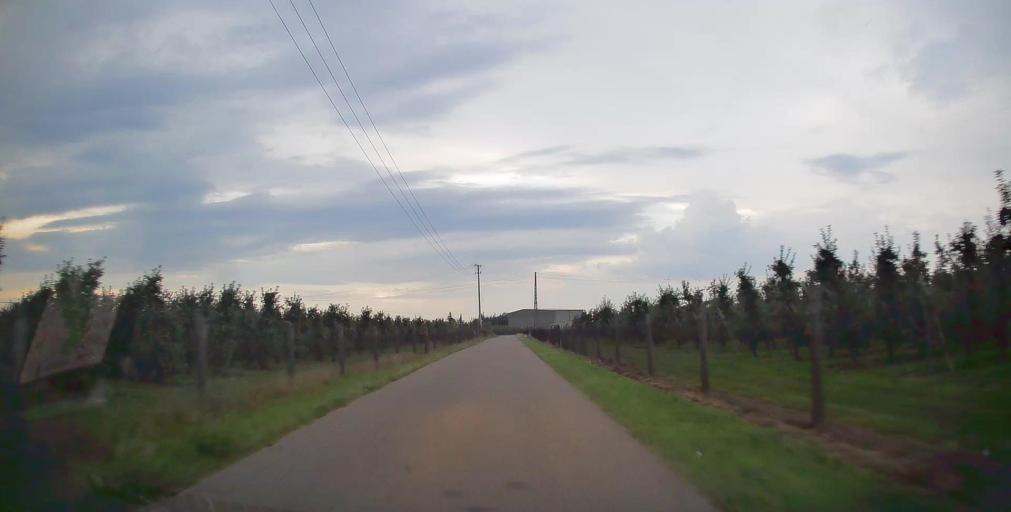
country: PL
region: Masovian Voivodeship
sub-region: Powiat grojecki
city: Jasieniec
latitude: 51.7897
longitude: 20.8968
